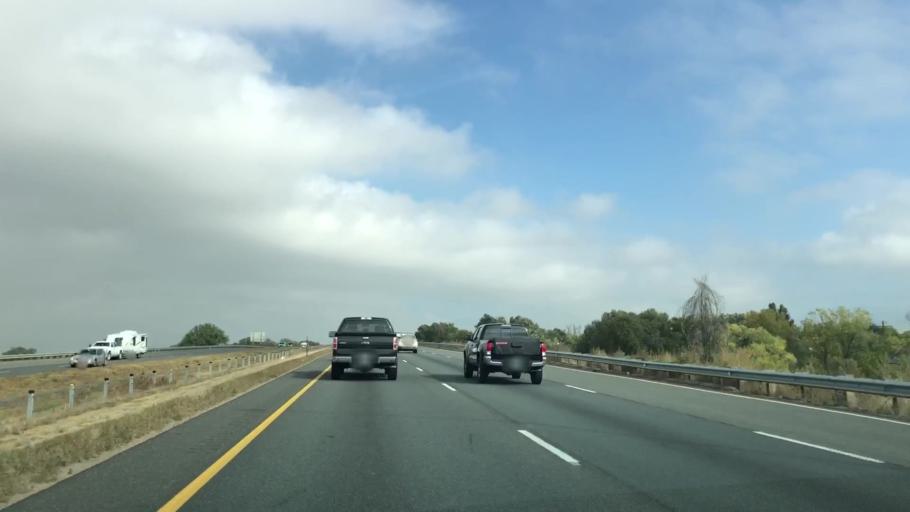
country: US
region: Colorado
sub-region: Larimer County
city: Fort Collins
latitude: 40.5370
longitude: -104.9940
